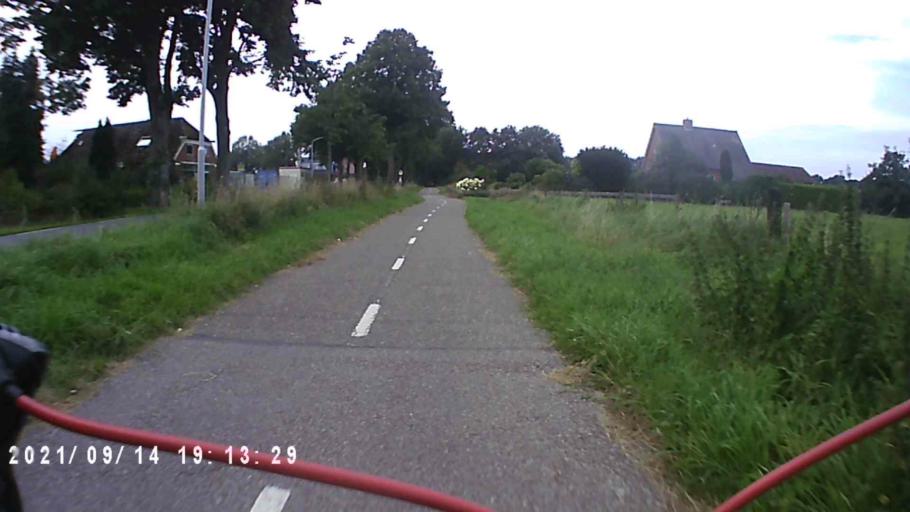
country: NL
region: Drenthe
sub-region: Gemeente Aa en Hunze
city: Anloo
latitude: 53.0662
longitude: 6.7092
